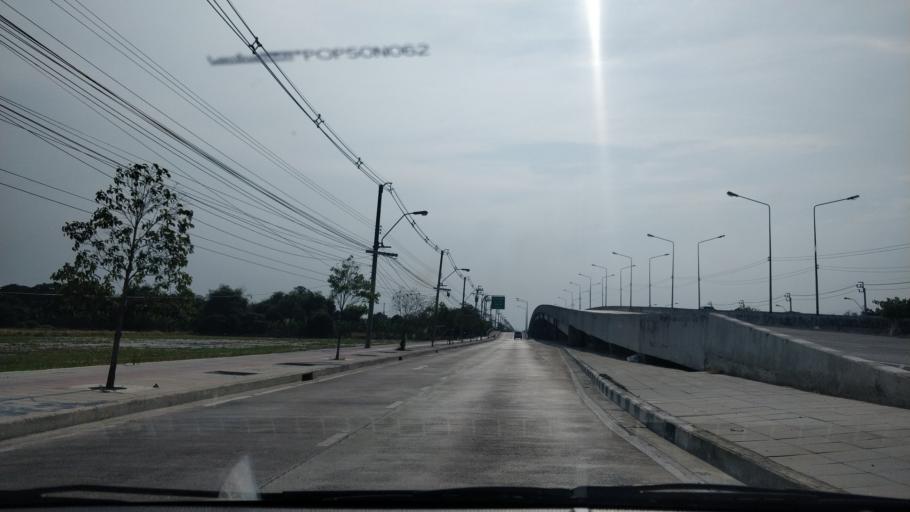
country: TH
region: Bangkok
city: Lat Krabang
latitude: 13.7556
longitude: 100.7411
